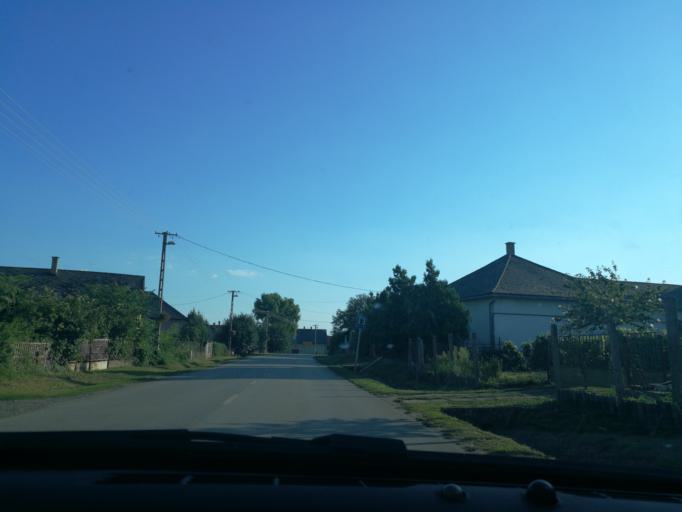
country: HU
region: Szabolcs-Szatmar-Bereg
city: Buj
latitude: 48.0978
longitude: 21.6461
